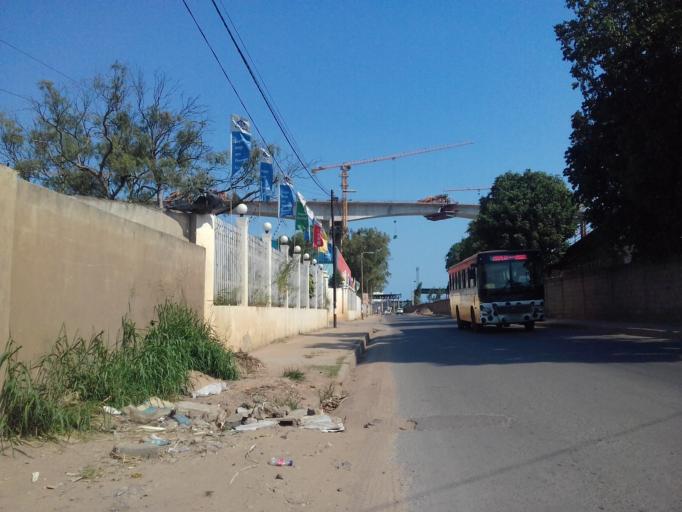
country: MZ
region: Maputo City
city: Maputo
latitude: -25.9639
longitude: 32.5581
